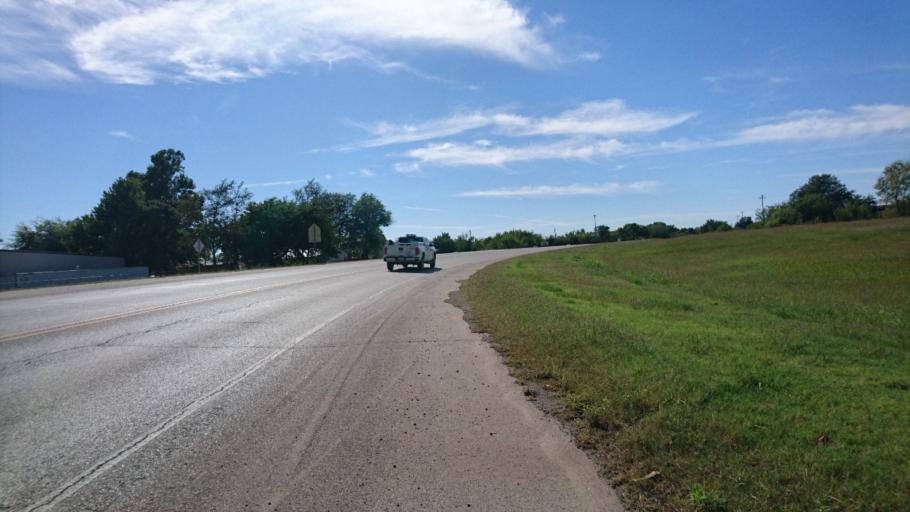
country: US
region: Oklahoma
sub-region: Lincoln County
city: Chandler
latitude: 35.7101
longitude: -96.7664
